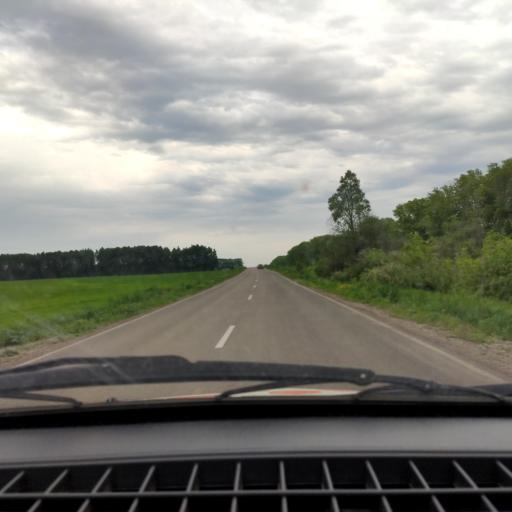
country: RU
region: Bashkortostan
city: Avdon
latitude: 54.5335
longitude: 55.7648
